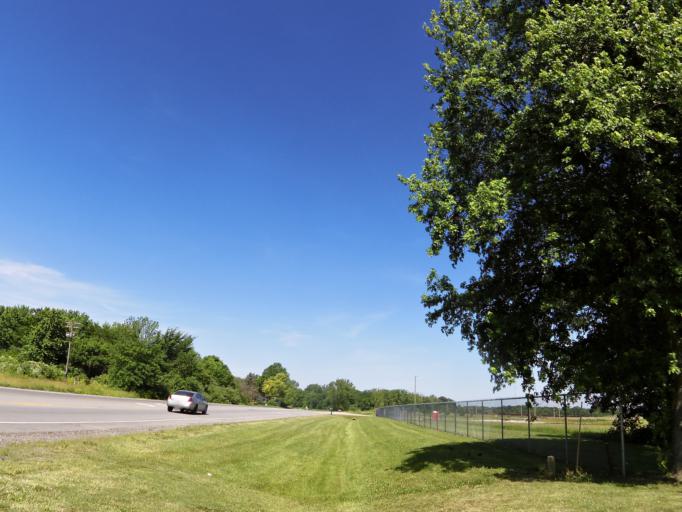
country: US
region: Illinois
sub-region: Vermilion County
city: Danville
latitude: 40.1334
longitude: -87.5580
